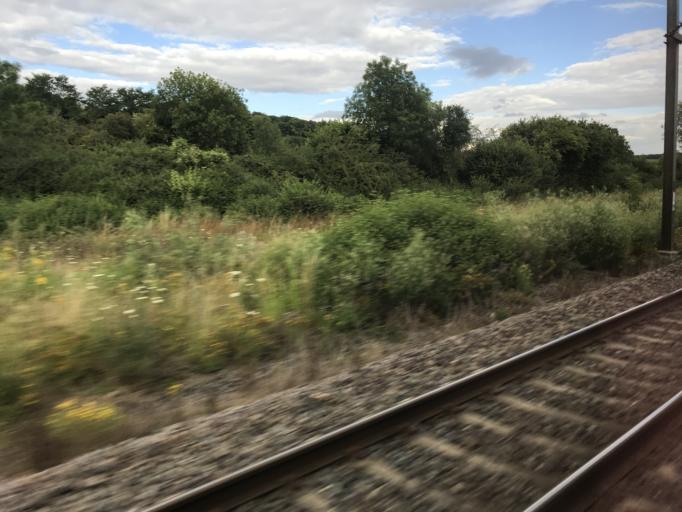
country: FR
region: Lorraine
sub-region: Departement de la Meuse
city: Stenay
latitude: 49.5435
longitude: 5.2372
